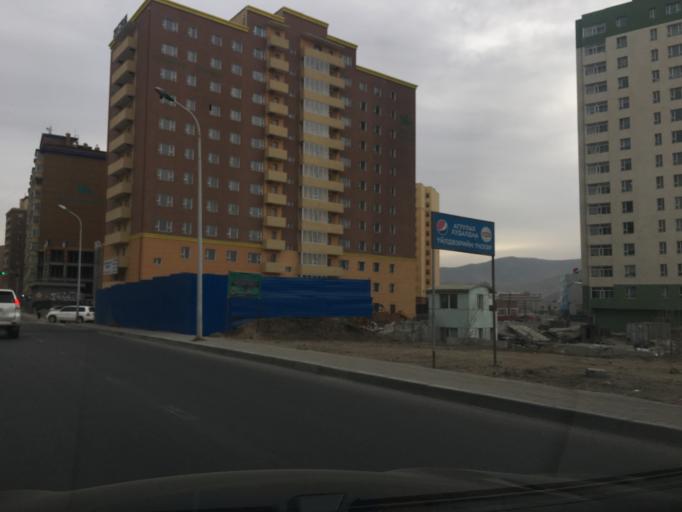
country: MN
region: Ulaanbaatar
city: Ulaanbaatar
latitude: 47.9033
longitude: 106.8813
